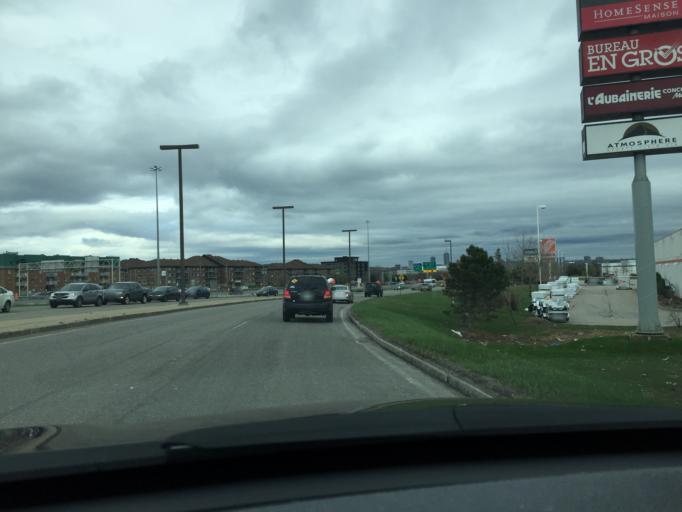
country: CA
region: Quebec
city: Quebec
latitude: 46.8442
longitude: -71.2725
